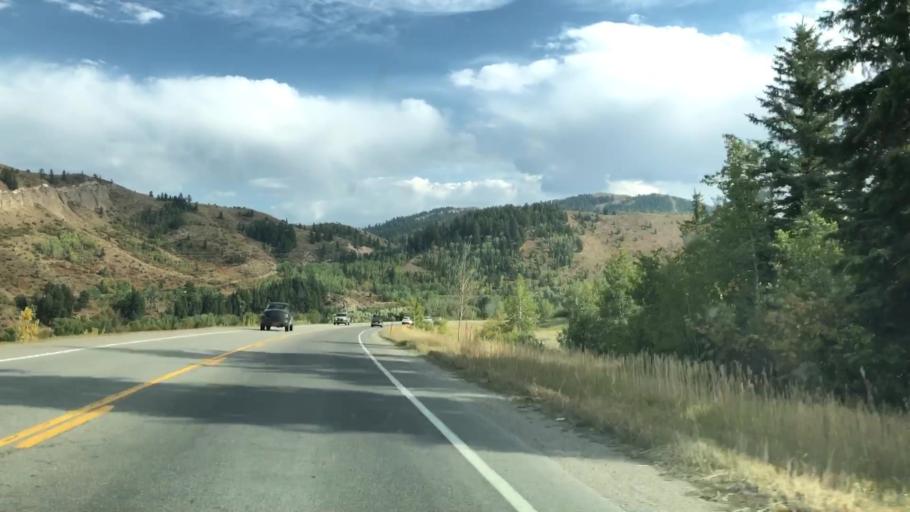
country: US
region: Wyoming
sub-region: Teton County
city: South Park
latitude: 43.3575
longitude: -110.7231
